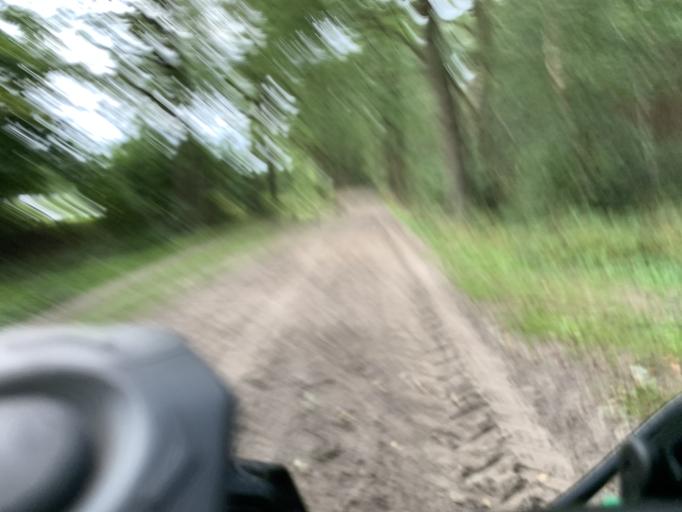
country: DE
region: Lower Saxony
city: Westerstede
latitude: 53.2342
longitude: 7.9172
